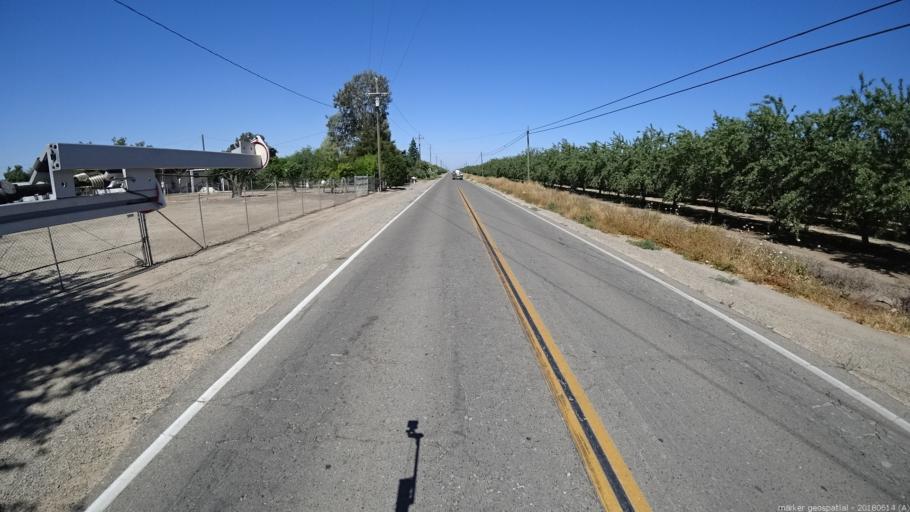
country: US
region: California
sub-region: Madera County
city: Fairmead
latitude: 36.9527
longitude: -120.2028
